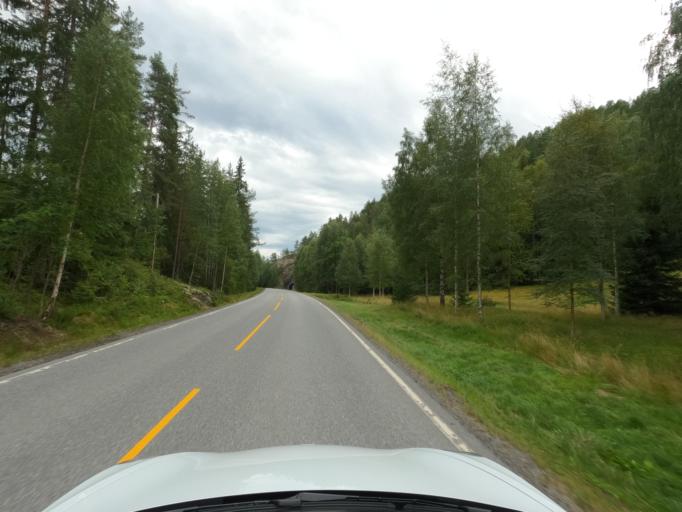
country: NO
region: Telemark
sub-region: Hjartdal
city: Sauland
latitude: 59.7385
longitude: 9.0201
